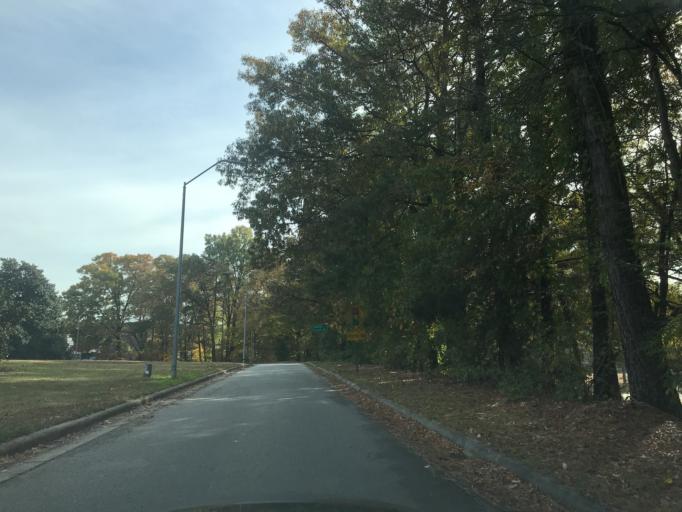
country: US
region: North Carolina
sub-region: Wake County
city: West Raleigh
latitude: 35.8002
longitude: -78.6620
